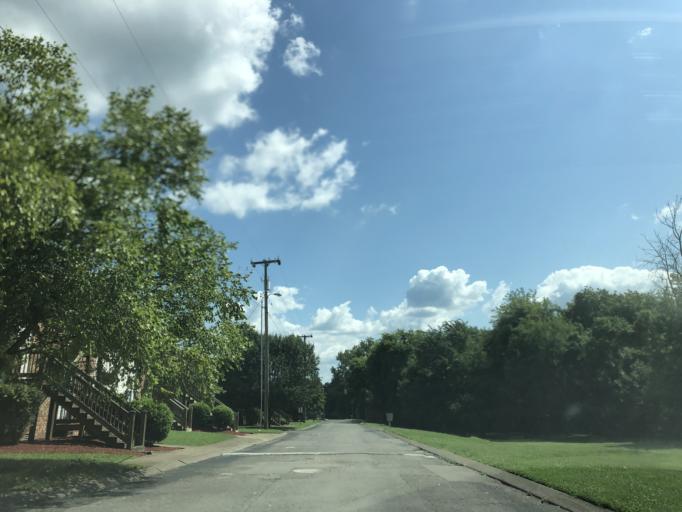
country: US
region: Tennessee
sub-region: Wilson County
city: Green Hill
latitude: 36.2105
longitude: -86.5905
